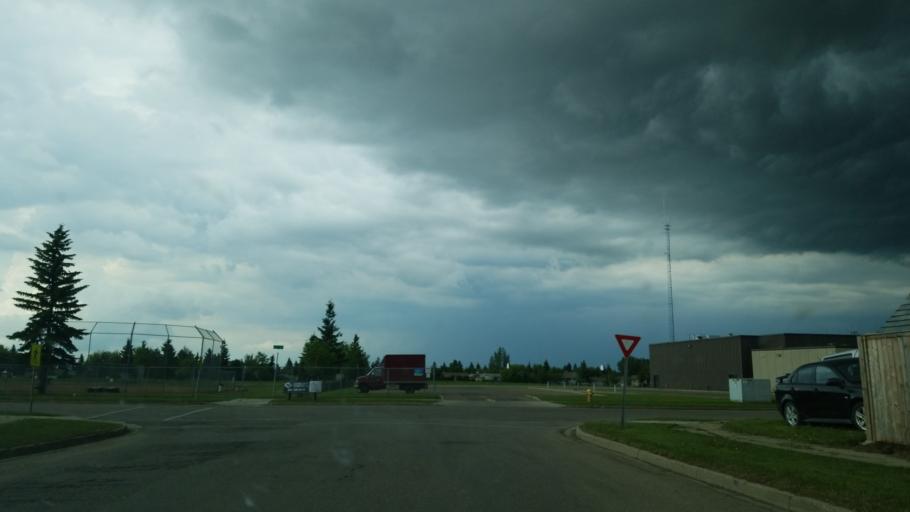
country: CA
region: Saskatchewan
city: Lloydminster
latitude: 53.2668
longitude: -110.0214
